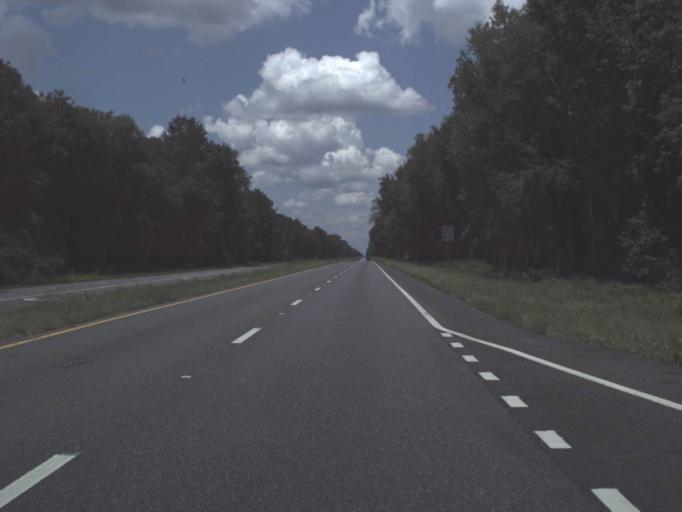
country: US
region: Florida
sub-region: Taylor County
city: Perry
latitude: 30.2023
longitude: -83.6565
